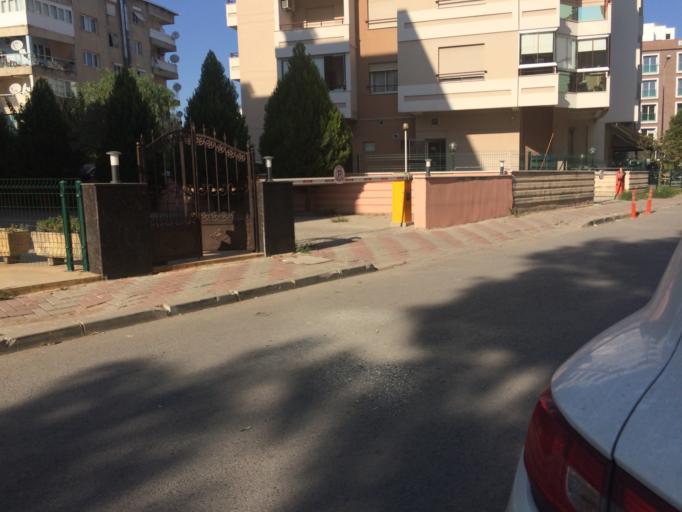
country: TR
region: Izmir
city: Karsiyaka
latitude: 38.4927
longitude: 27.0537
